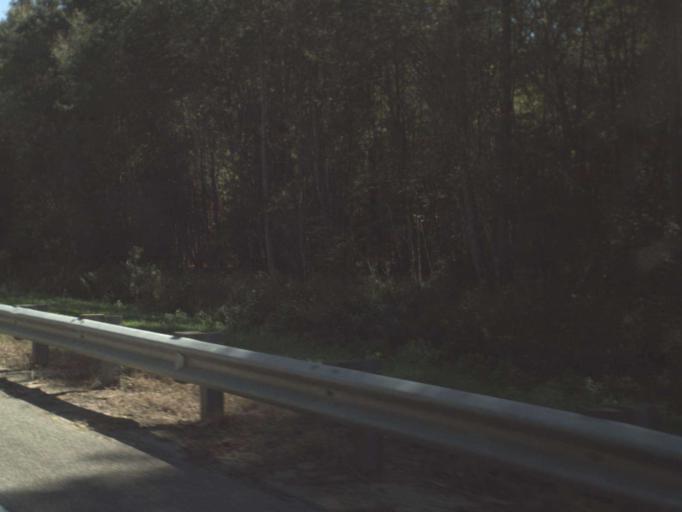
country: US
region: Florida
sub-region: Jefferson County
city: Monticello
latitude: 30.5316
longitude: -83.8122
